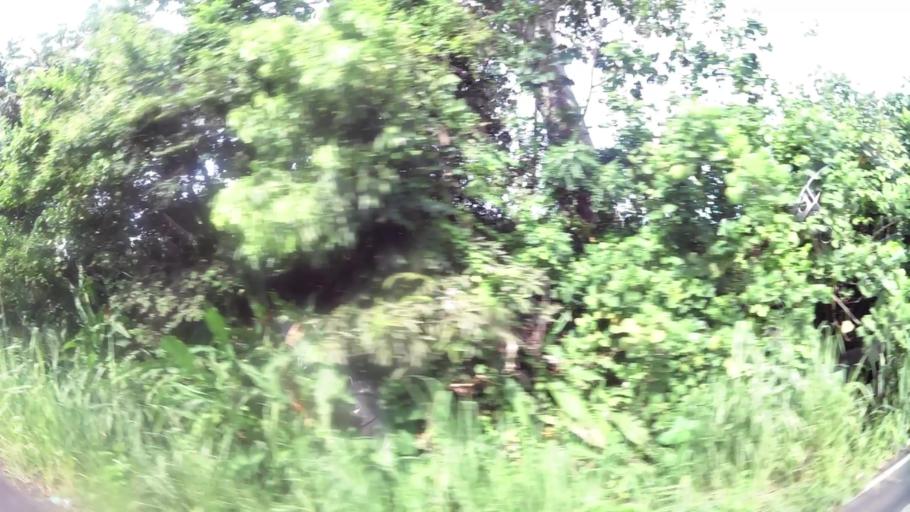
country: PA
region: Panama
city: La Chorrera
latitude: 8.8874
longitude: -79.7708
